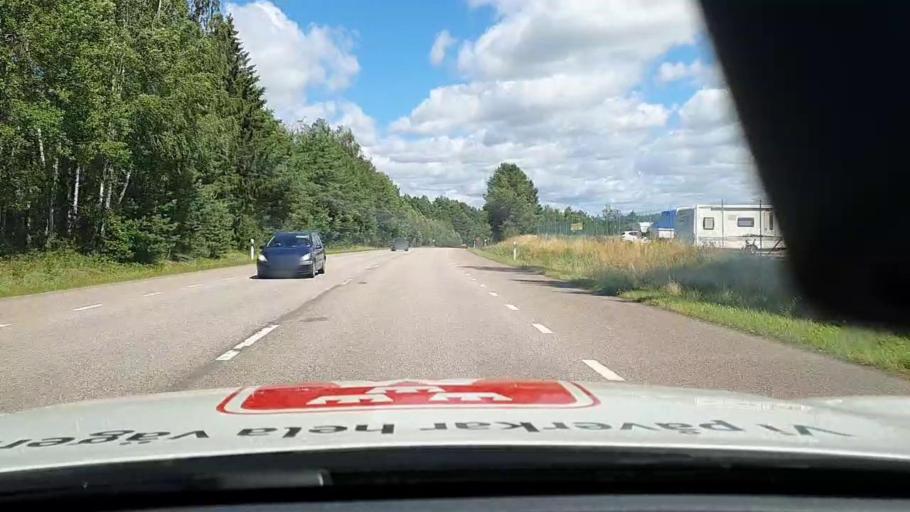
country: SE
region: Vaestra Goetaland
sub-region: Skovde Kommun
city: Stopen
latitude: 58.4325
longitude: 13.9198
